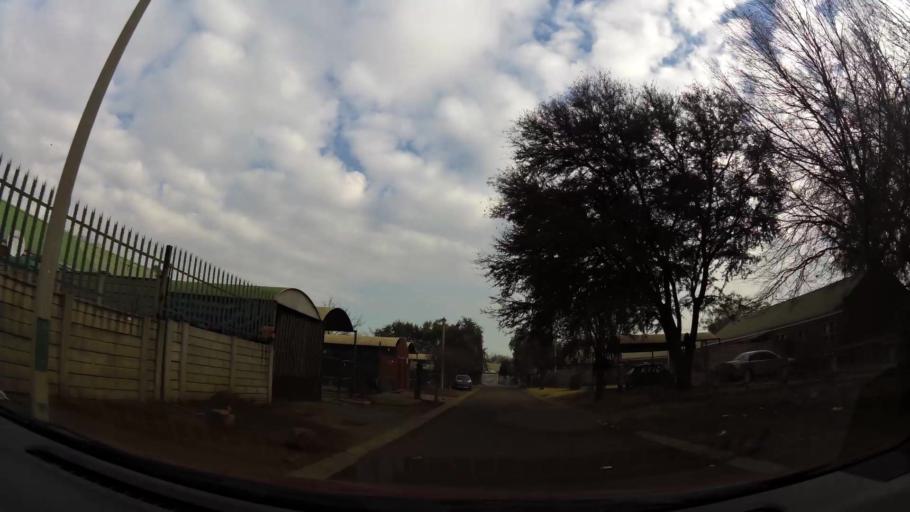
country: ZA
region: Gauteng
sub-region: Sedibeng District Municipality
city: Vanderbijlpark
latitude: -26.6825
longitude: 27.8150
